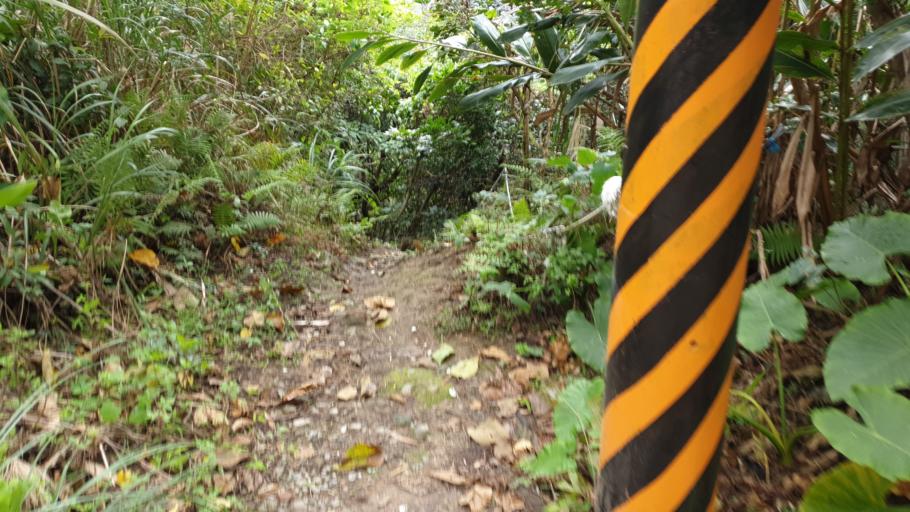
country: TW
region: Taipei
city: Taipei
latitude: 25.0906
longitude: 121.5464
